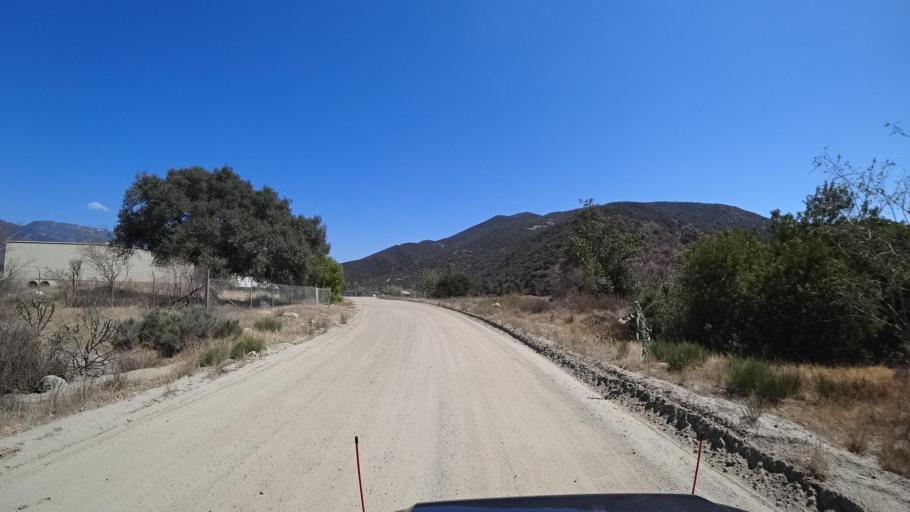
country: US
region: California
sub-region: San Diego County
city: Rainbow
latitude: 33.3630
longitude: -117.0624
